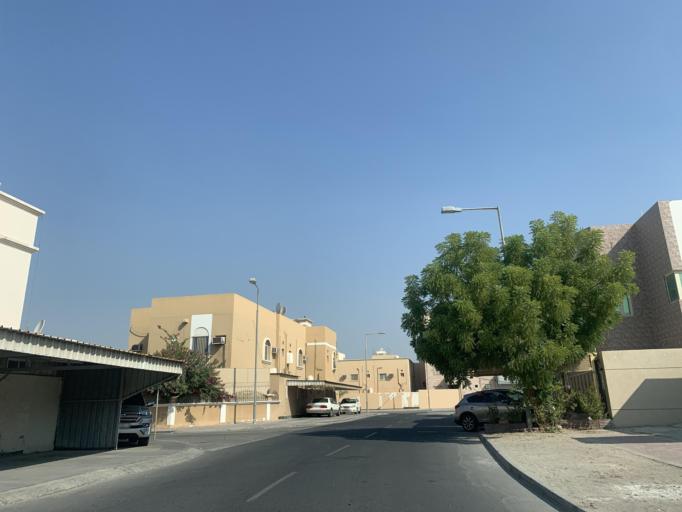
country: BH
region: Central Governorate
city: Madinat Hamad
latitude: 26.1034
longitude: 50.5061
